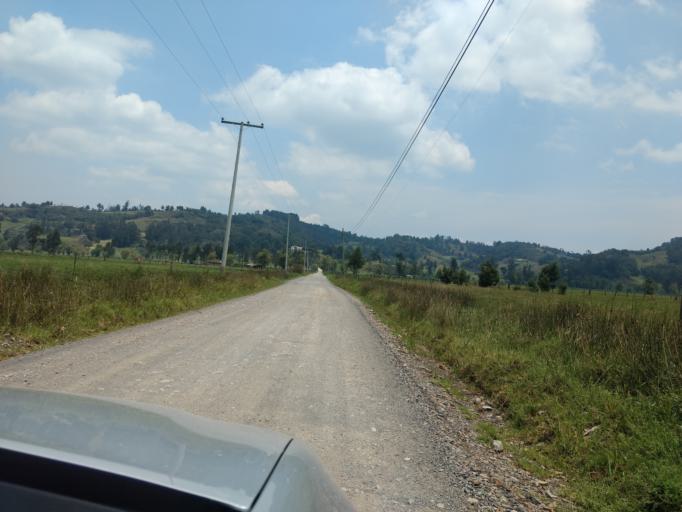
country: CO
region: Boyaca
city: Raquira
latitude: 5.4982
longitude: -73.7110
